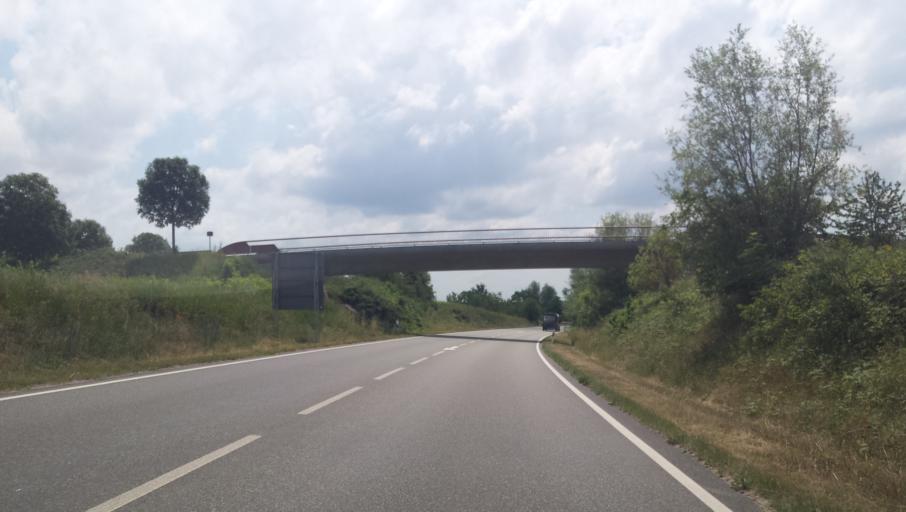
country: DE
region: Rheinland-Pfalz
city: Niederkirchen bei Deidesheim
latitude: 49.4330
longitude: 8.2024
